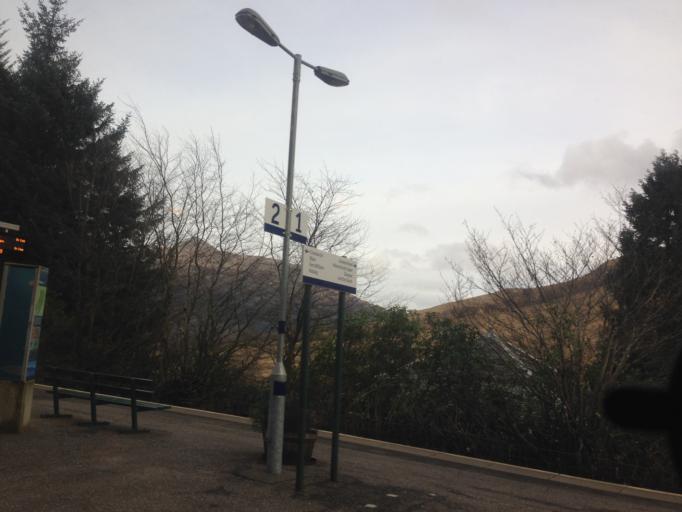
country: GB
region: Scotland
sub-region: Argyll and Bute
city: Garelochhead
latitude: 56.2031
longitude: -4.7234
